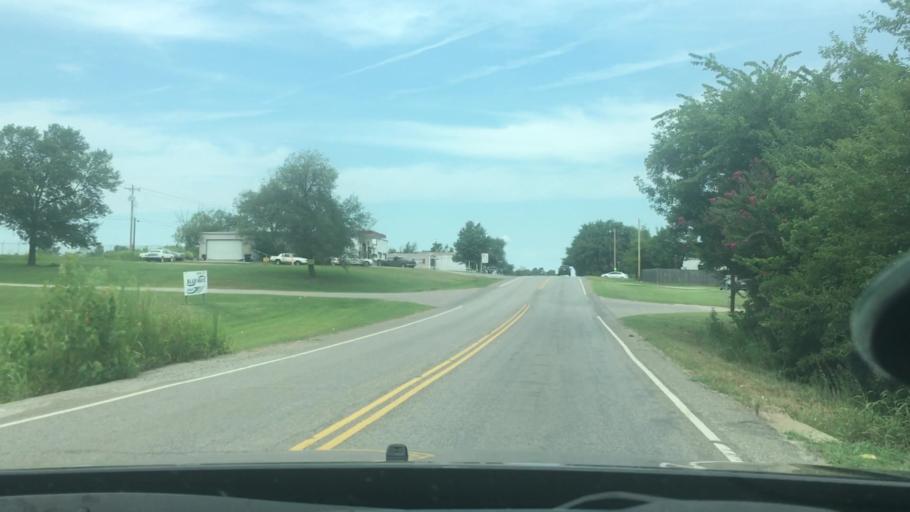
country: US
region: Oklahoma
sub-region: Seminole County
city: Seminole
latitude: 35.2291
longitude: -96.6836
